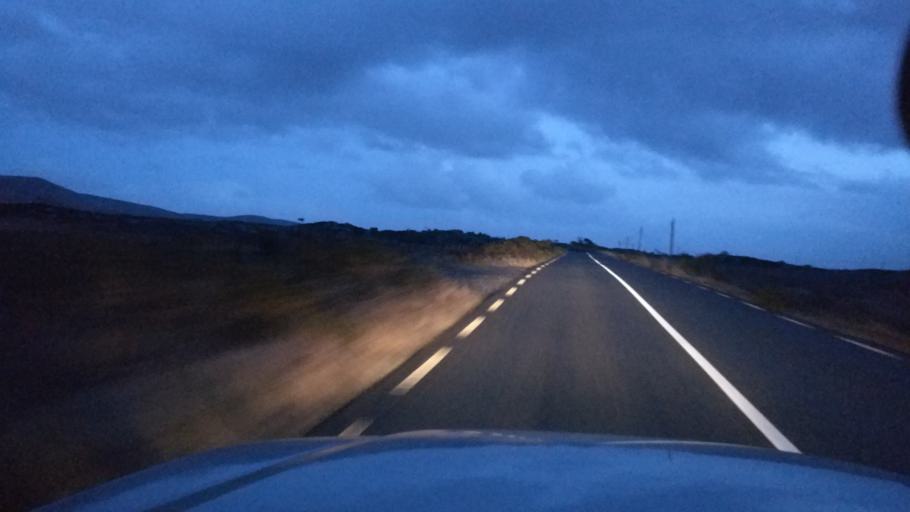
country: IE
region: Connaught
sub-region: County Galway
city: Oughterard
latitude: 53.3942
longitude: -9.5473
